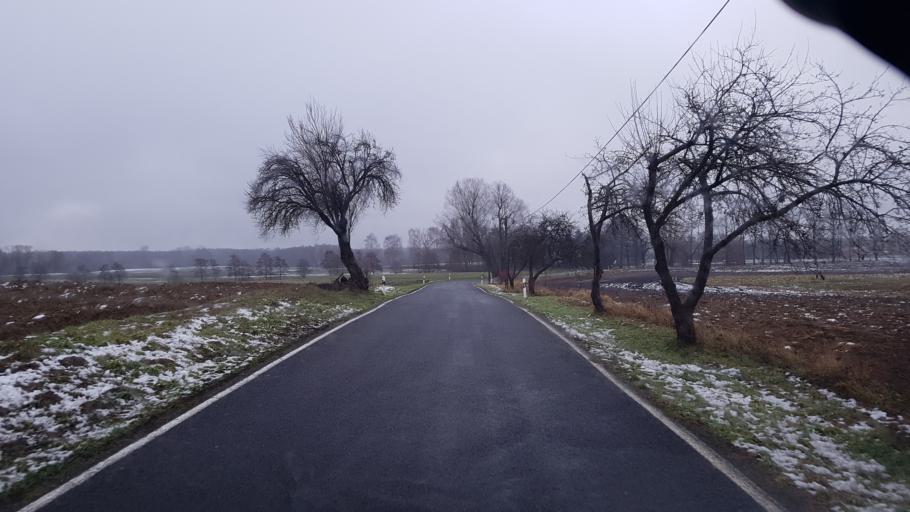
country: DE
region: Brandenburg
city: Lieberose
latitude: 51.9791
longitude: 14.3175
